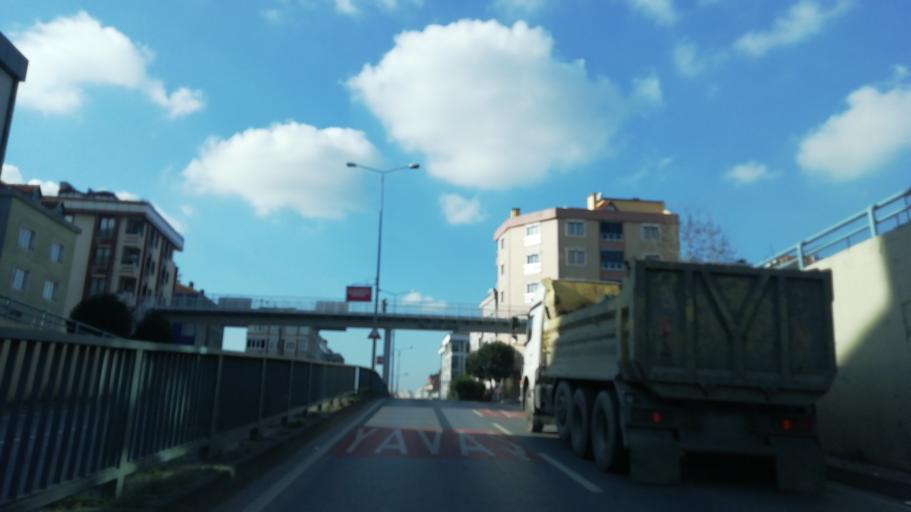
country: TR
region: Istanbul
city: Esenler
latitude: 41.0597
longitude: 28.8999
